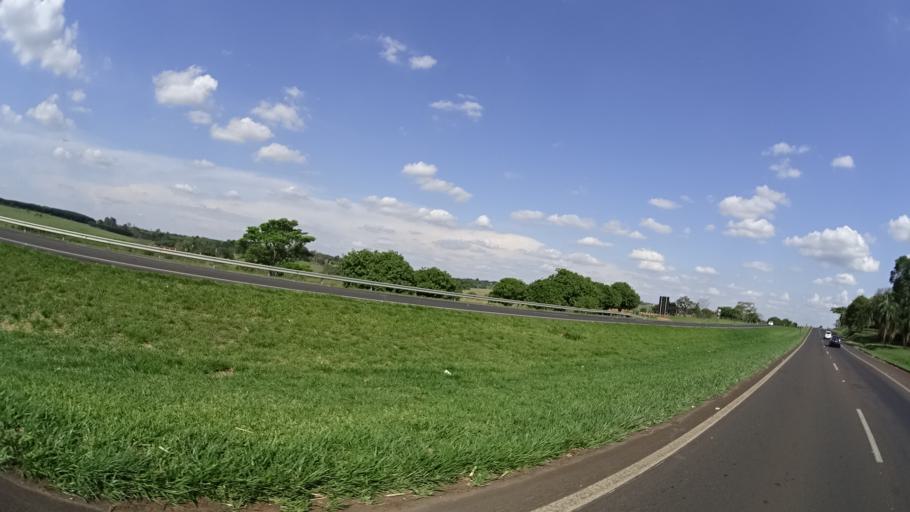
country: BR
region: Sao Paulo
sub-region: Sao Jose Do Rio Preto
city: Sao Jose do Rio Preto
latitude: -20.8937
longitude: -49.3058
